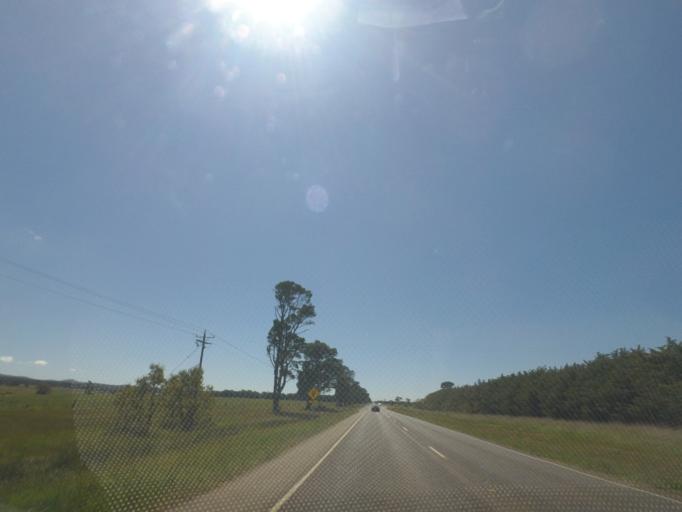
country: AU
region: Victoria
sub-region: Hume
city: Sunbury
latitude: -37.3909
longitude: 144.7478
